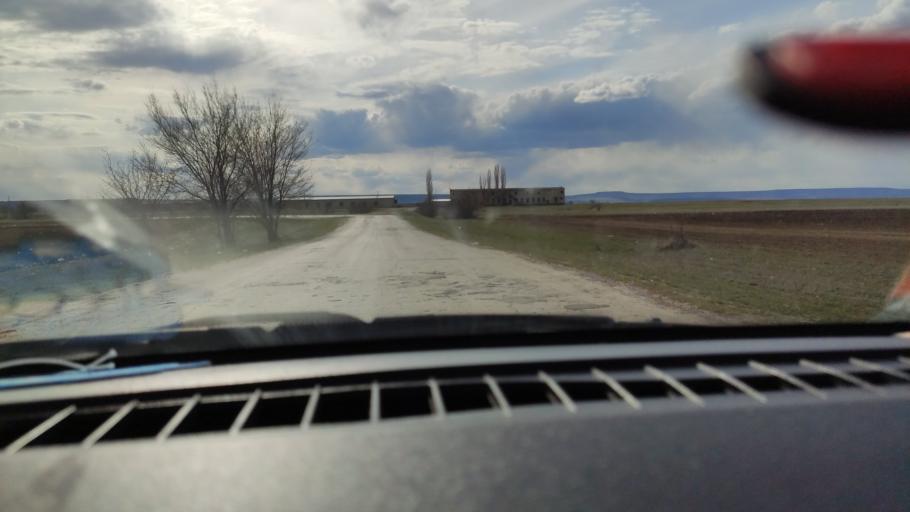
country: RU
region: Saratov
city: Rovnoye
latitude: 50.9366
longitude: 46.0944
